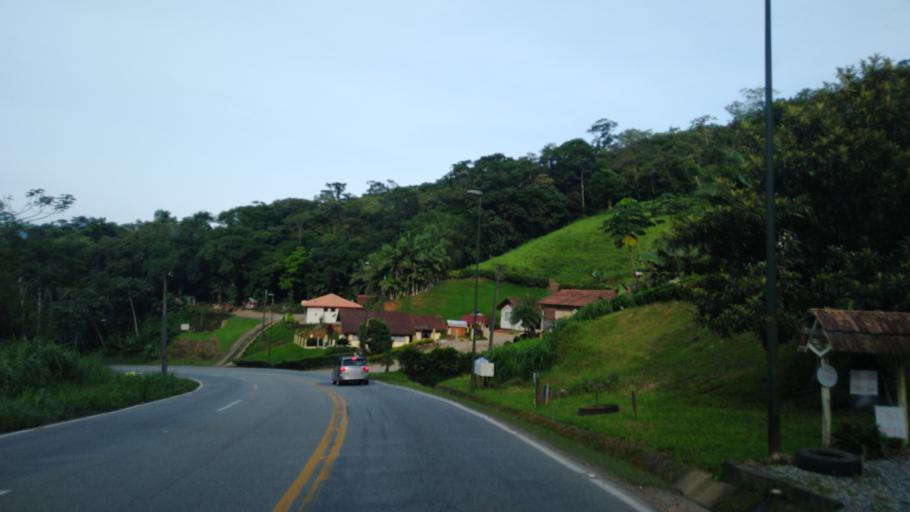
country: BR
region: Santa Catarina
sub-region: Joinville
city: Joinville
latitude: -26.1824
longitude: -49.0169
